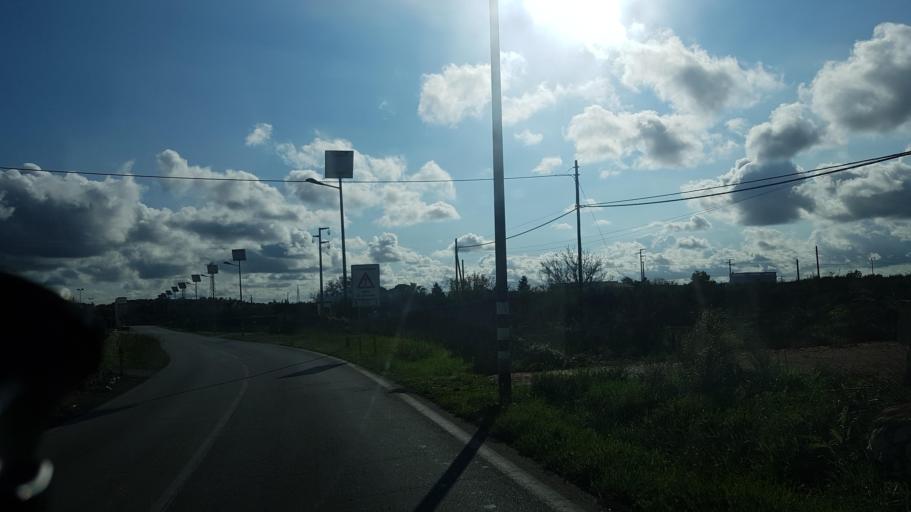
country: IT
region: Apulia
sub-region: Provincia di Brindisi
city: Ostuni
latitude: 40.7126
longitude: 17.5779
